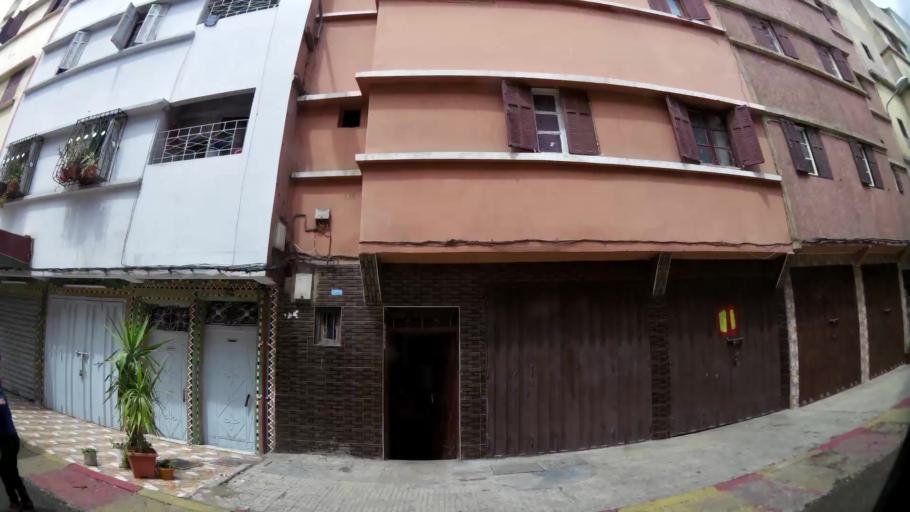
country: MA
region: Grand Casablanca
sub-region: Mediouna
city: Tit Mellil
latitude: 33.6051
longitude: -7.5120
